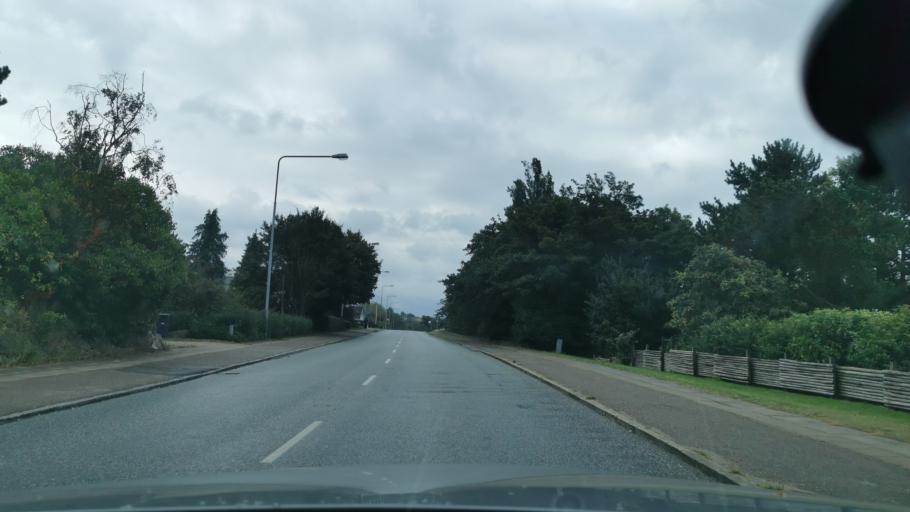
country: DK
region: Zealand
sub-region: Kalundborg Kommune
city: Kalundborg
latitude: 55.7012
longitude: 11.0291
